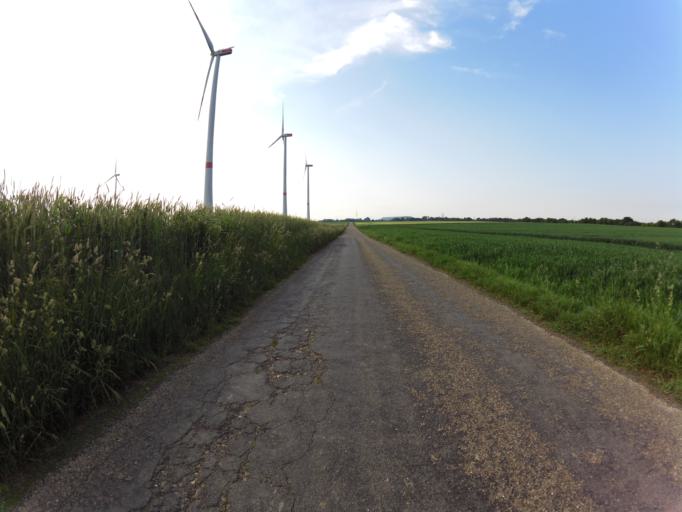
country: DE
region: North Rhine-Westphalia
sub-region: Regierungsbezirk Koln
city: Linnich
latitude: 50.9793
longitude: 6.2032
